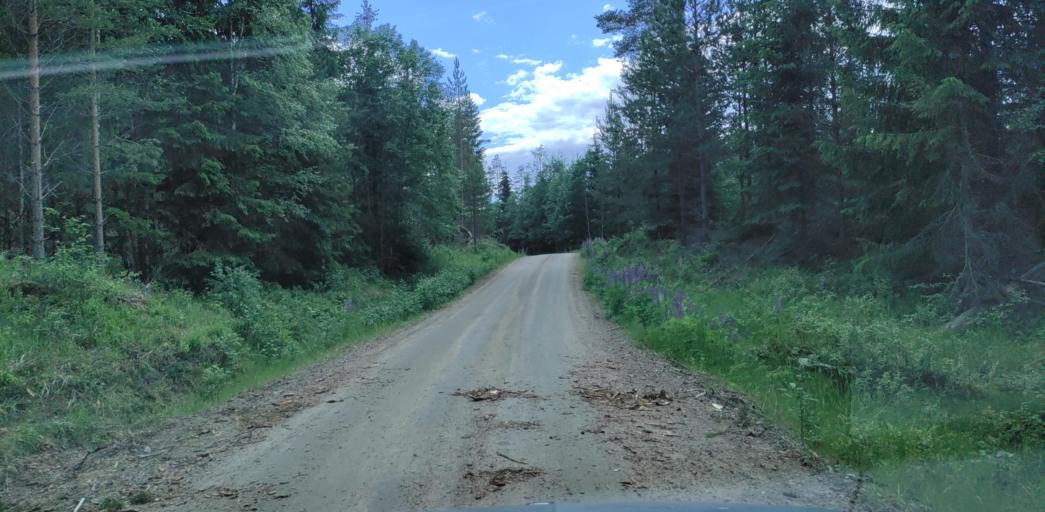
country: SE
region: Vaermland
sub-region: Hagfors Kommun
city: Ekshaerad
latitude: 60.0763
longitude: 13.2917
